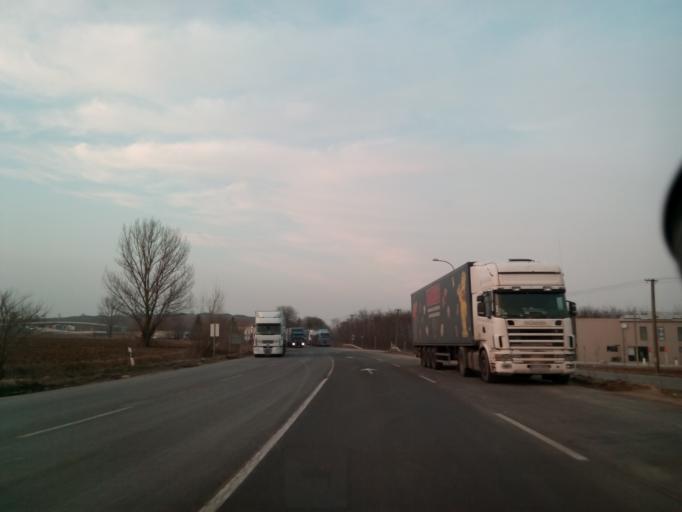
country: HU
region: Borsod-Abauj-Zemplen
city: Gonc
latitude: 48.5278
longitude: 21.2541
